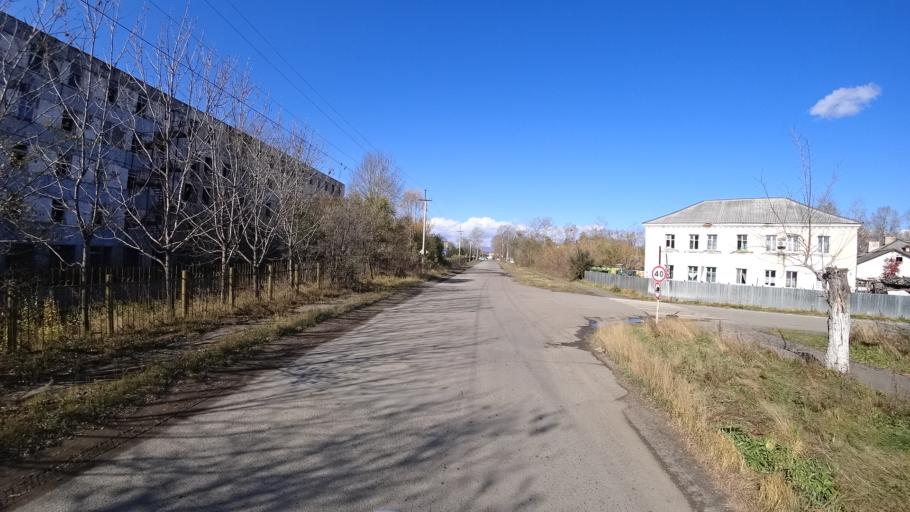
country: RU
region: Khabarovsk Krai
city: Amursk
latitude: 50.0976
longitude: 136.4943
